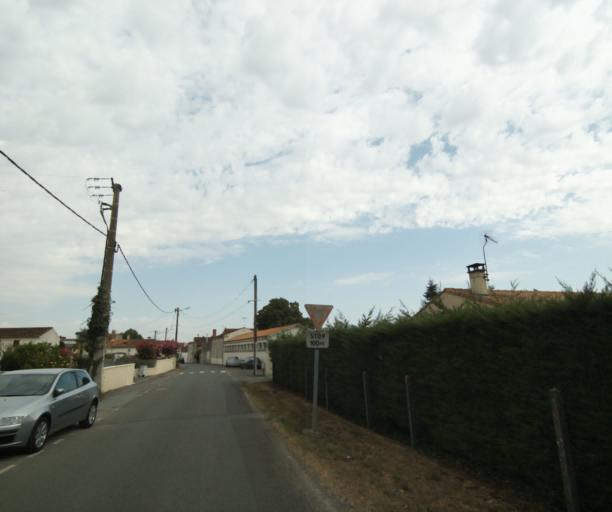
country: FR
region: Poitou-Charentes
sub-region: Departement de la Charente-Maritime
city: Tonnay-Charente
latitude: 45.9649
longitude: -0.8722
